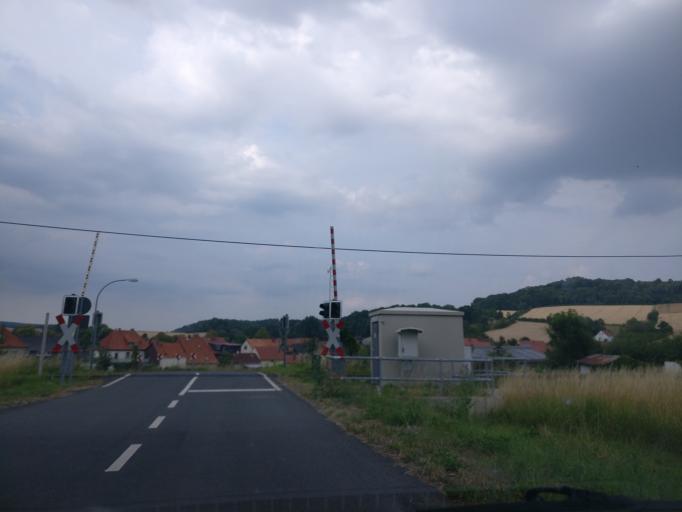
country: DE
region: Lower Saxony
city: Adelebsen
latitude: 51.5932
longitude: 9.7813
